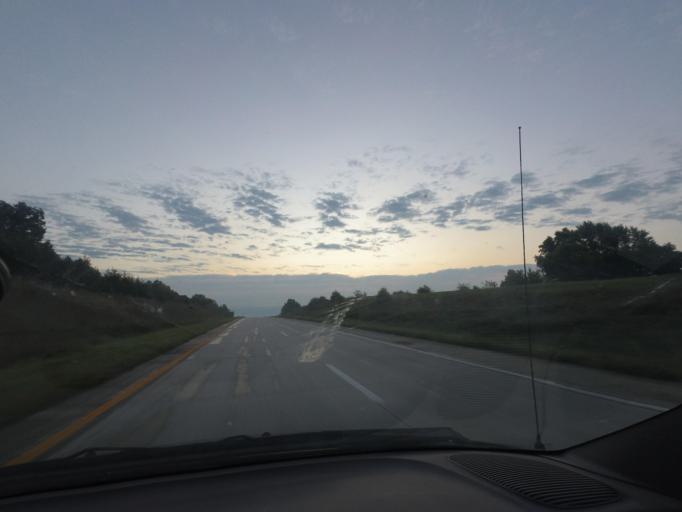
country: US
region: Missouri
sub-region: Macon County
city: Macon
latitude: 39.7561
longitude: -92.6078
